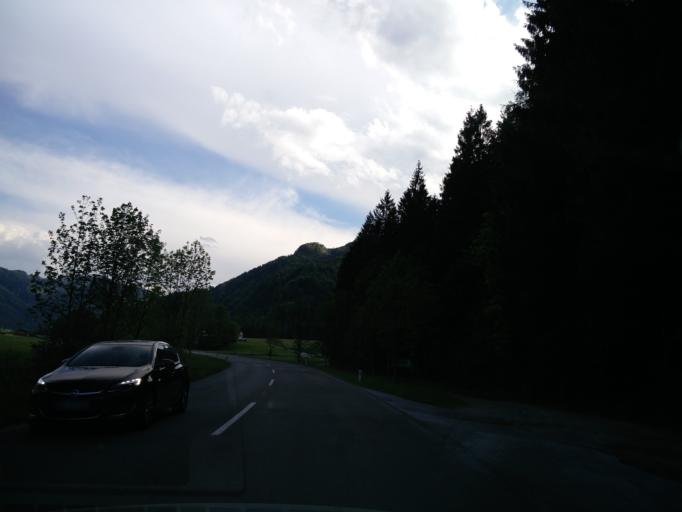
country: AT
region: Tyrol
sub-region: Politischer Bezirk Kitzbuhel
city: Kirchdorf in Tirol
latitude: 47.6053
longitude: 12.4673
